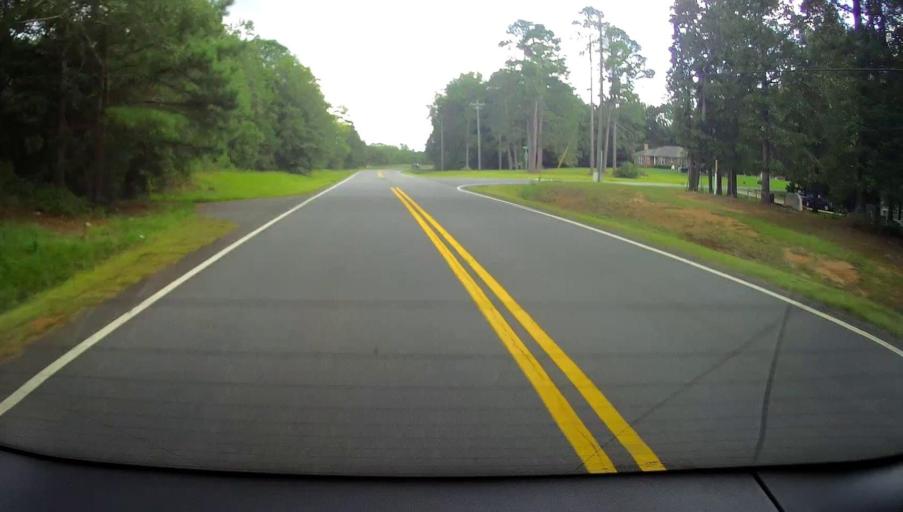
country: US
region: Georgia
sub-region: Monroe County
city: Forsyth
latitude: 32.8817
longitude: -83.9323
